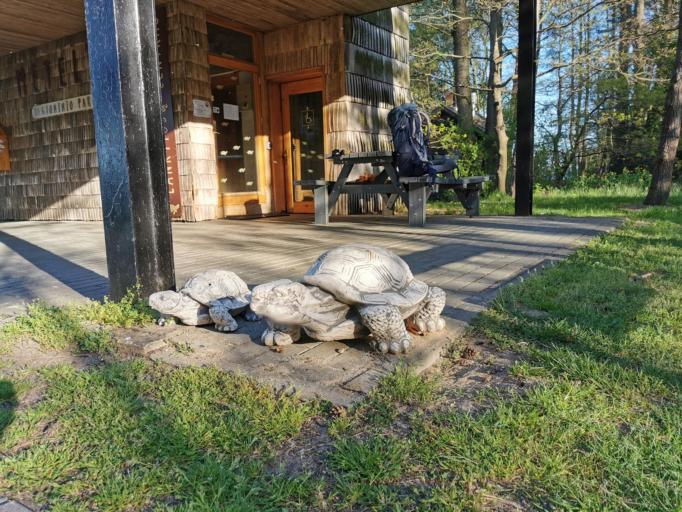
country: LT
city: Simnas
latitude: 54.2836
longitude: 23.7410
